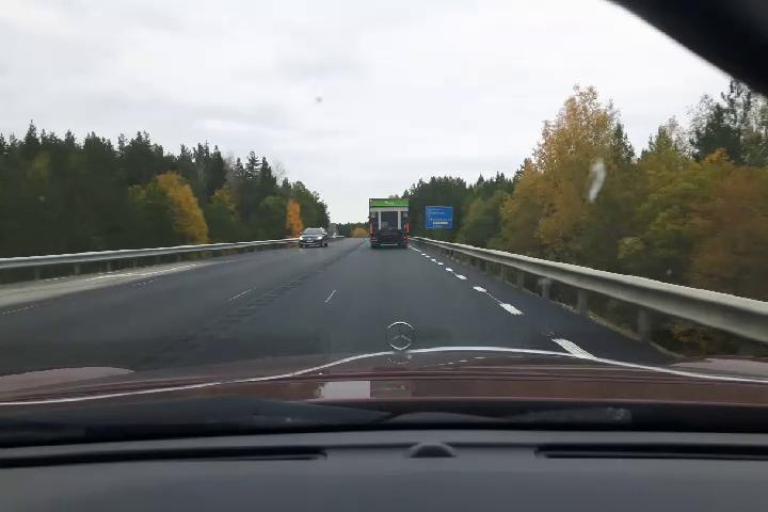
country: SE
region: Soedermanland
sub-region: Strangnas Kommun
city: Strangnas
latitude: 59.4083
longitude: 17.0205
